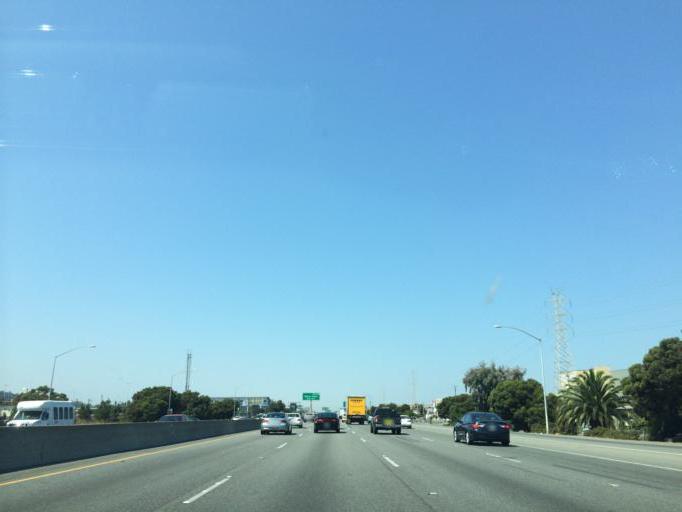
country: US
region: California
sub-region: San Mateo County
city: San Carlos
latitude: 37.5159
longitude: -122.2582
